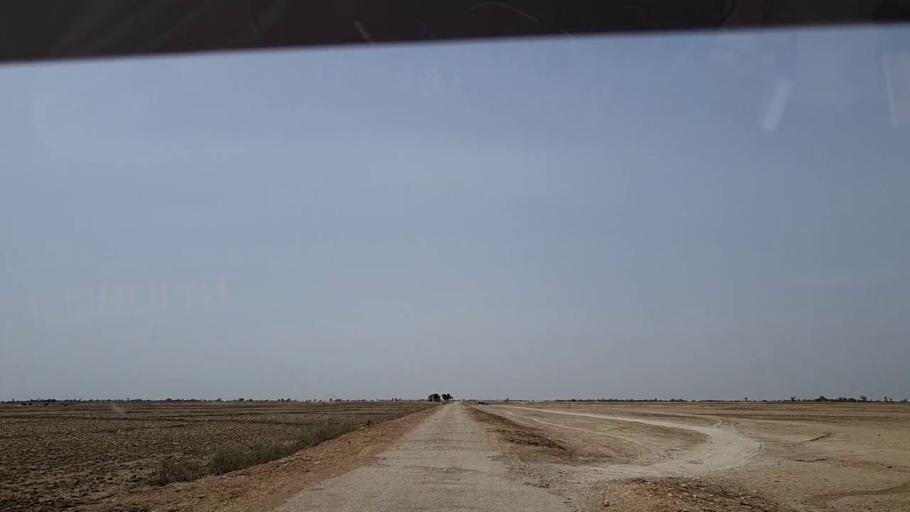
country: PK
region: Sindh
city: Johi
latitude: 26.7278
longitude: 67.6403
